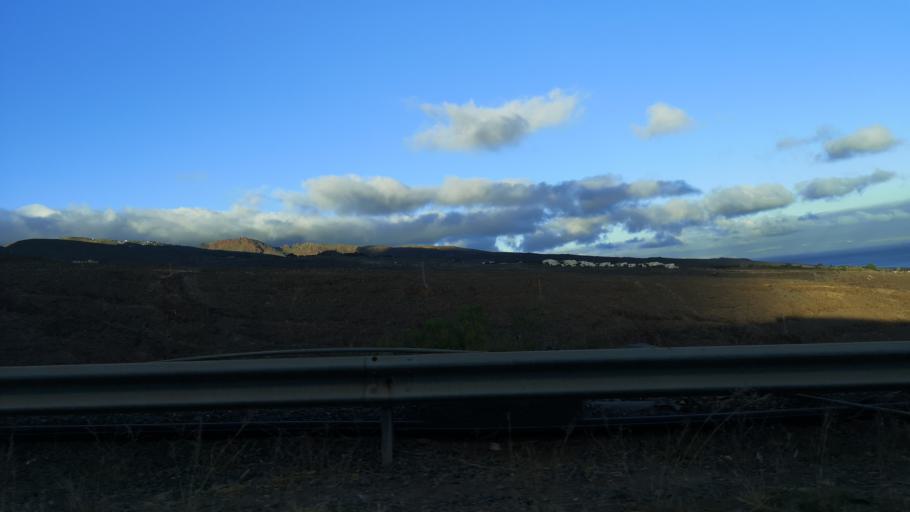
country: ES
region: Canary Islands
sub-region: Provincia de Santa Cruz de Tenerife
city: Alajero
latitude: 28.0335
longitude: -17.2111
